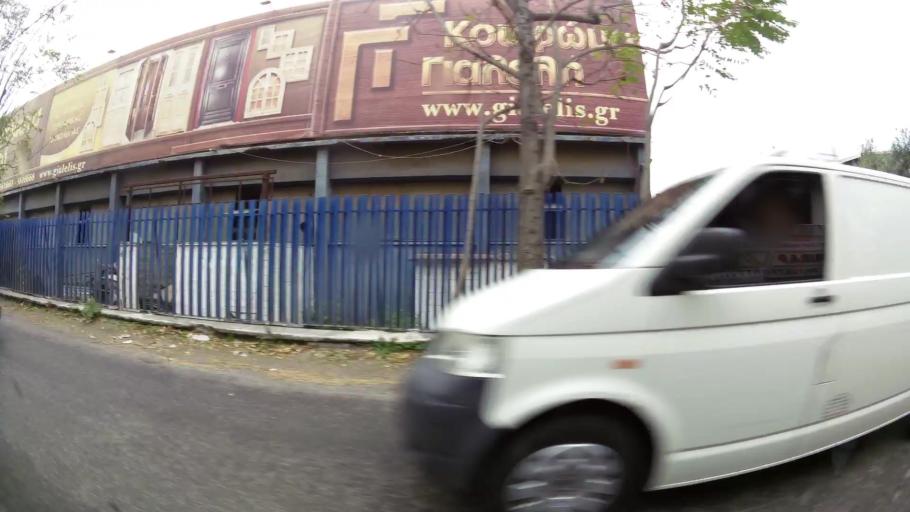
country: GR
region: Attica
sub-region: Nomarchia Athinas
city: Aigaleo
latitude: 37.9790
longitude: 23.6876
